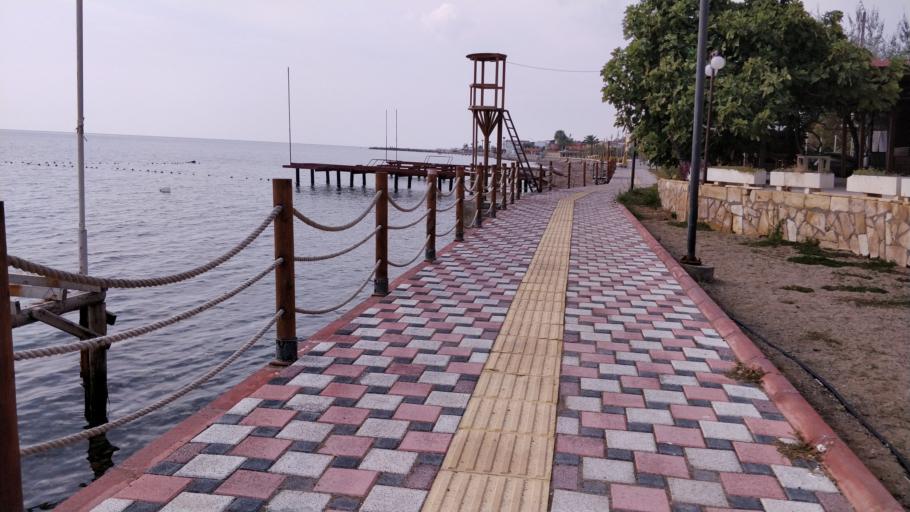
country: TR
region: Canakkale
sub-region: Merkez
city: Kucukkuyu
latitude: 39.5467
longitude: 26.6146
